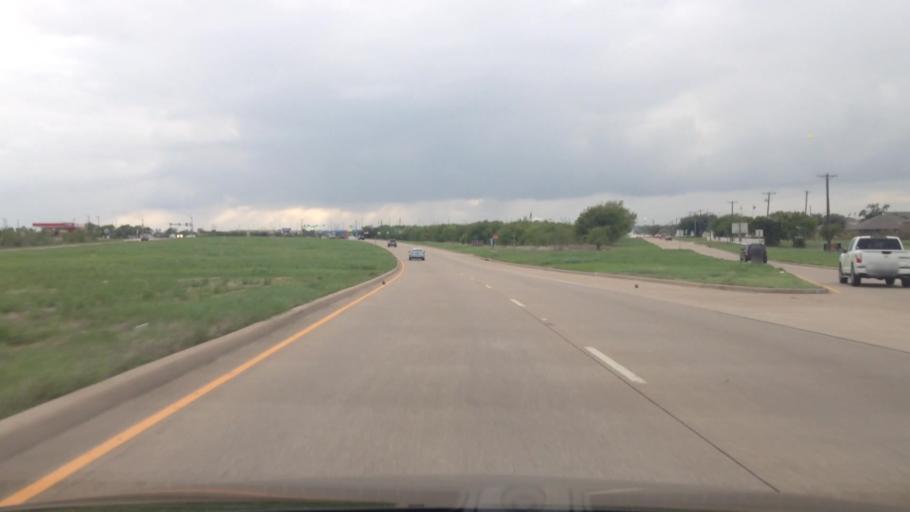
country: US
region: Texas
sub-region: Tarrant County
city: Crowley
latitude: 32.5777
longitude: -97.3300
